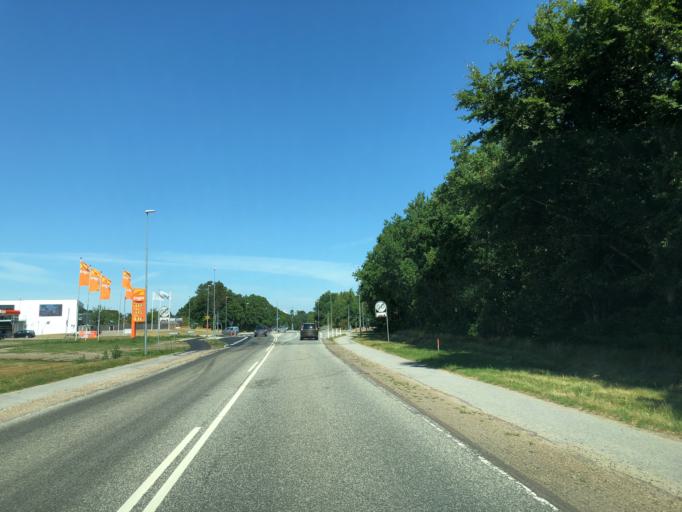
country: DK
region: Central Jutland
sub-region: Skive Kommune
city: Skive
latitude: 56.5525
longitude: 9.0250
